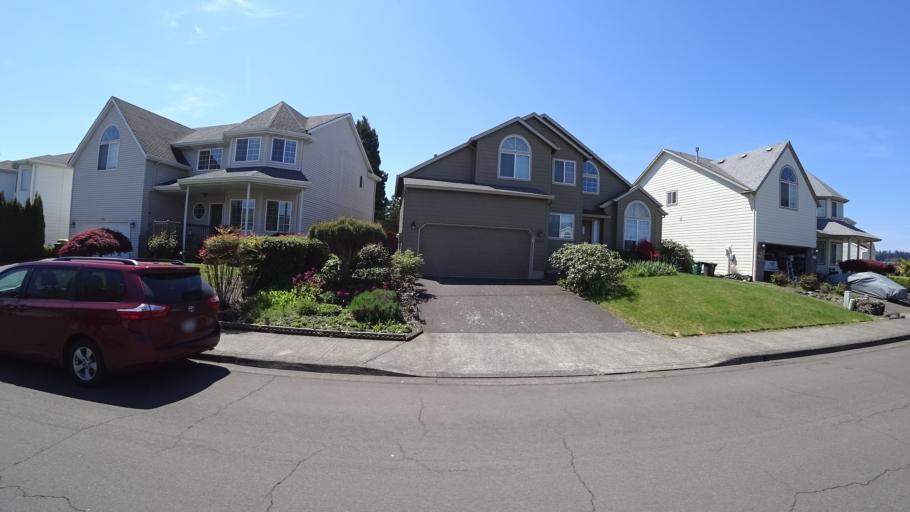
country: US
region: Oregon
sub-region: Washington County
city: King City
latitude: 45.4311
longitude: -122.8167
